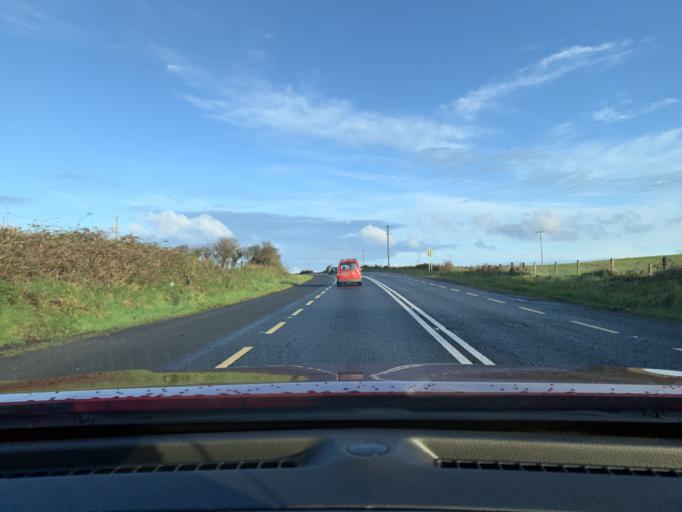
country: IE
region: Connaught
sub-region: Sligo
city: Sligo
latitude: 54.3638
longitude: -8.5271
